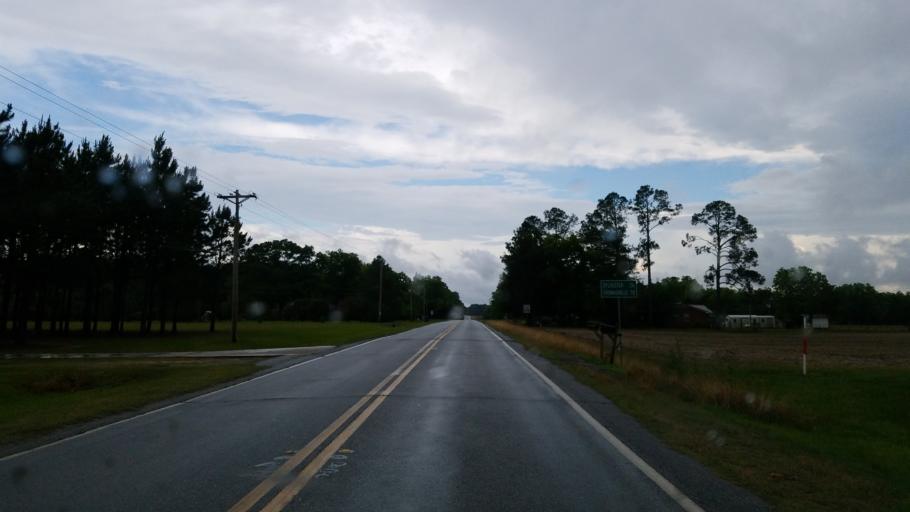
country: US
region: Georgia
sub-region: Crisp County
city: Cordele
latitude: 31.9034
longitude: -83.7670
